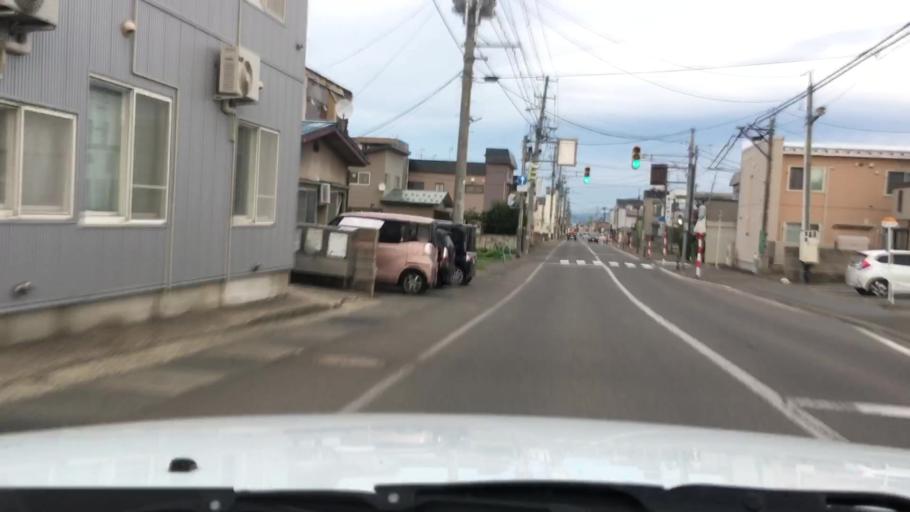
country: JP
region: Aomori
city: Hirosaki
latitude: 40.5868
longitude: 140.4773
